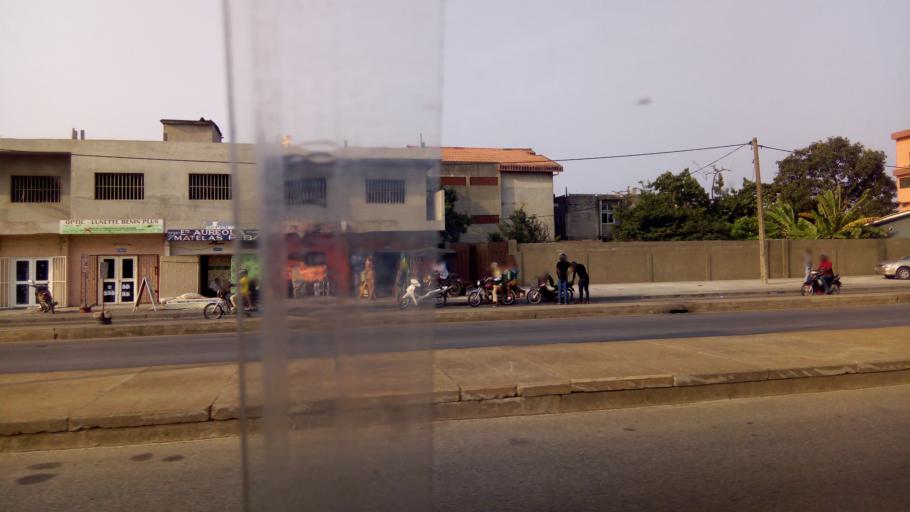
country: BJ
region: Littoral
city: Cotonou
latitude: 6.3878
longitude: 2.3668
